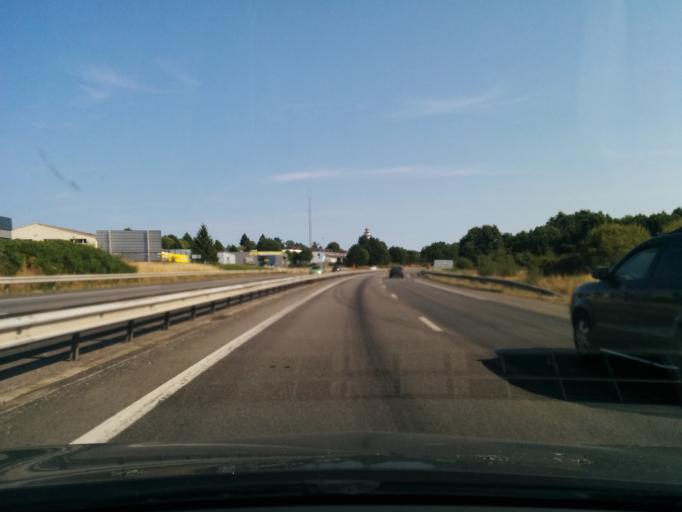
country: FR
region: Limousin
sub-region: Departement de la Haute-Vienne
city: Condat-sur-Vienne
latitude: 45.7935
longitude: 1.3015
